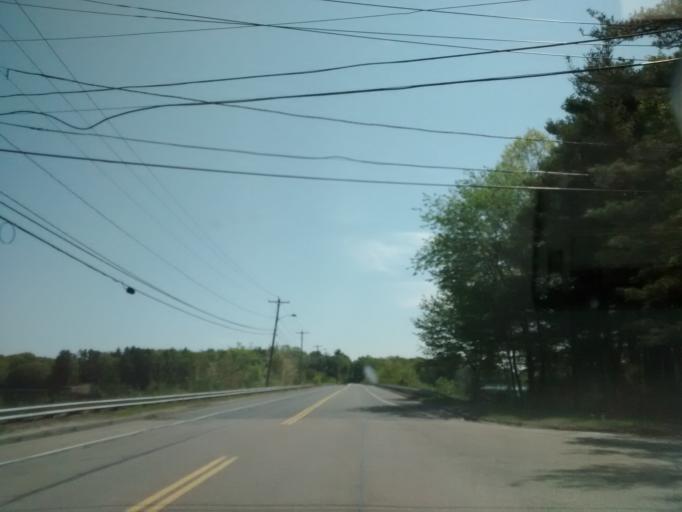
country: US
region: Massachusetts
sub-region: Worcester County
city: Whitinsville
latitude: 42.1102
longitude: -71.6921
